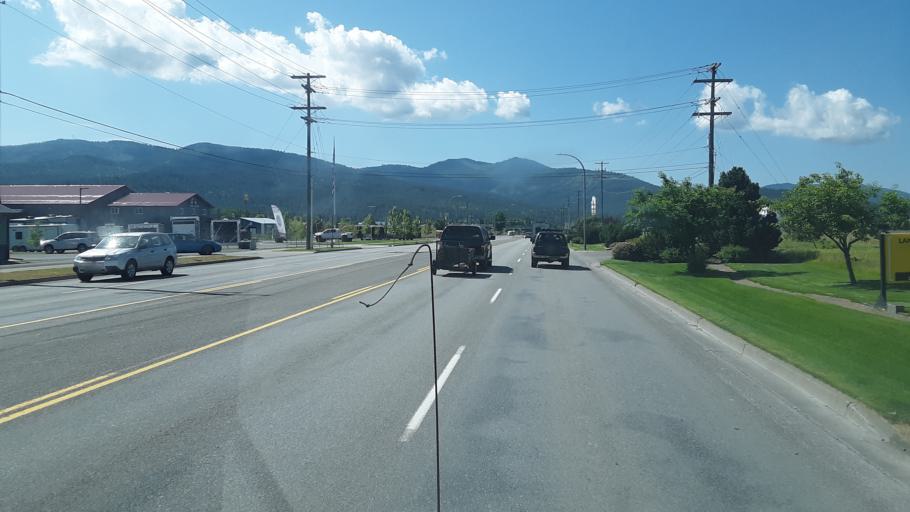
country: US
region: Idaho
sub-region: Kootenai County
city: Post Falls
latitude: 47.7151
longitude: -117.0018
